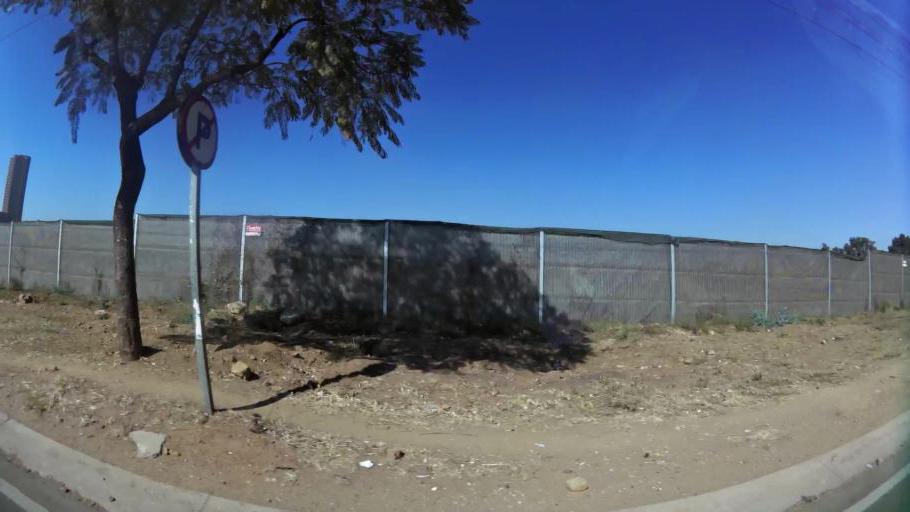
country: ZA
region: Gauteng
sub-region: City of Tshwane Metropolitan Municipality
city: Pretoria
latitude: -25.7430
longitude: 28.1743
